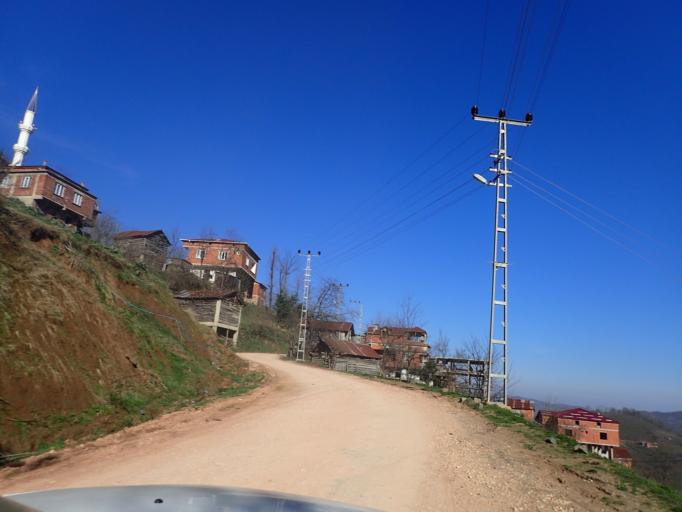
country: TR
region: Ordu
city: Camas
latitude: 40.8711
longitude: 37.5006
